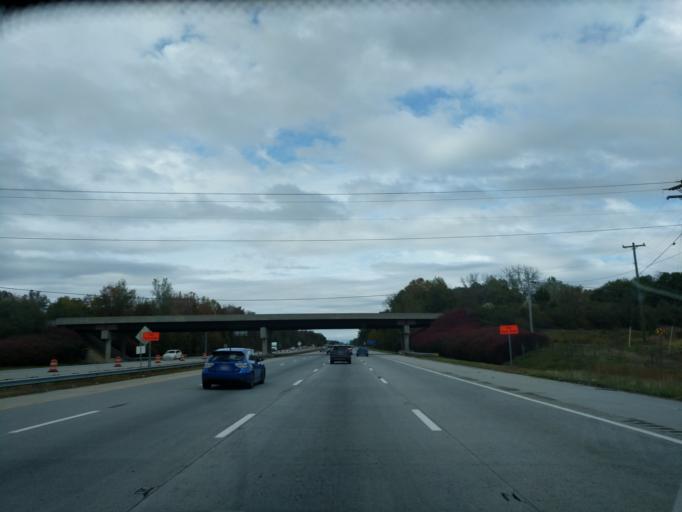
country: US
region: North Carolina
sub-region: Rowan County
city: China Grove
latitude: 35.5864
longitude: -80.5471
